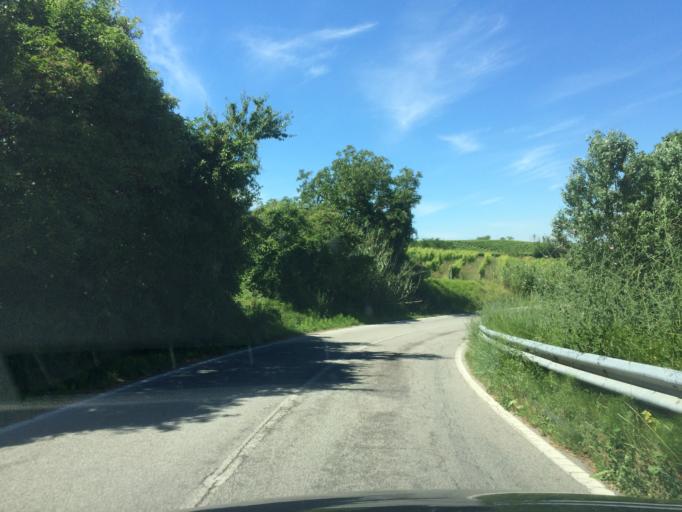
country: IT
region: Piedmont
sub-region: Provincia di Asti
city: Castel Boglione
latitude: 44.7327
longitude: 8.3910
